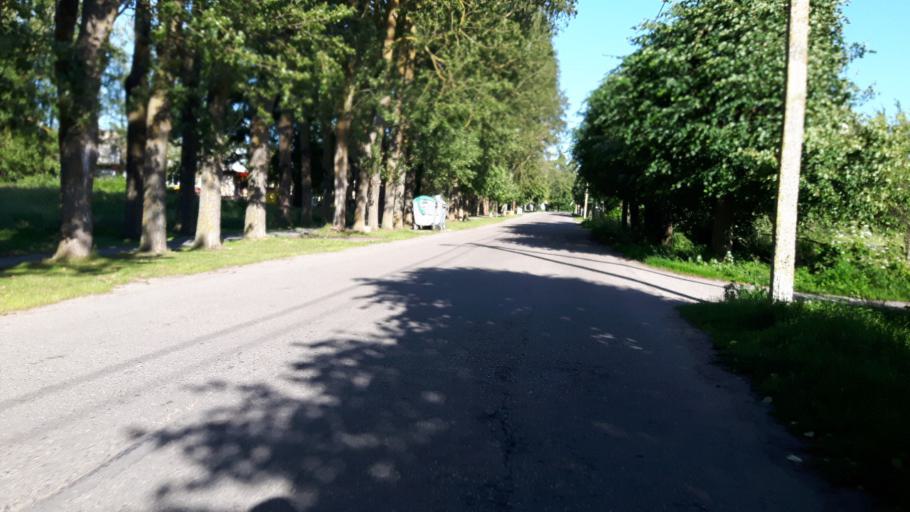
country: LT
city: Nida
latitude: 55.1562
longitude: 20.8473
